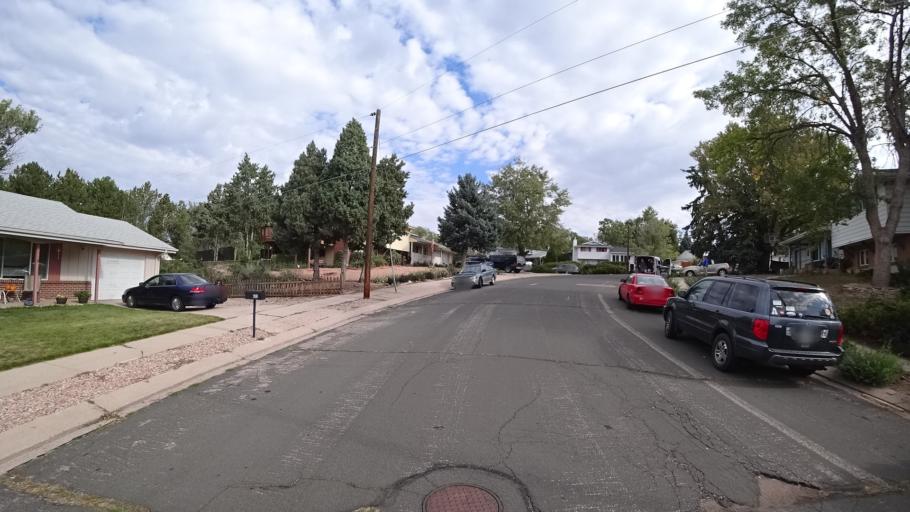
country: US
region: Colorado
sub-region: El Paso County
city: Cimarron Hills
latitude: 38.8430
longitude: -104.7539
